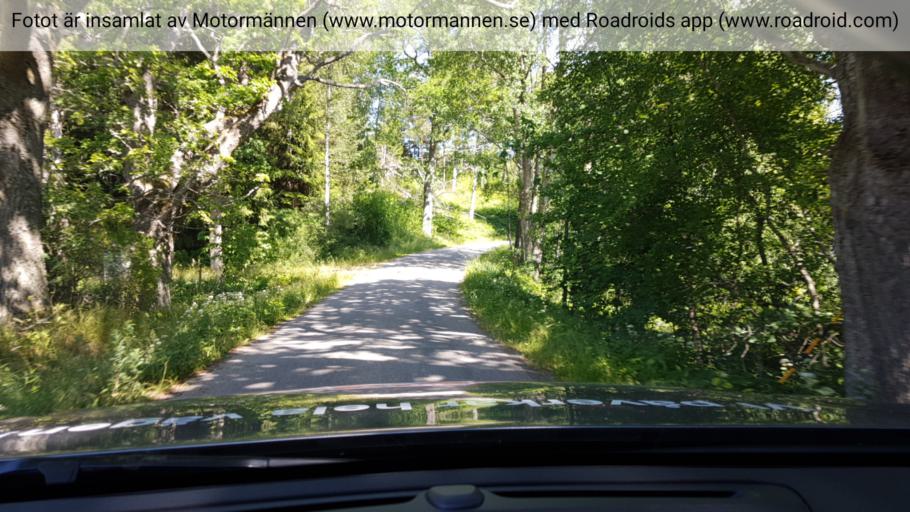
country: SE
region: Stockholm
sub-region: Haninge Kommun
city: Jordbro
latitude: 59.0150
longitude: 18.1140
